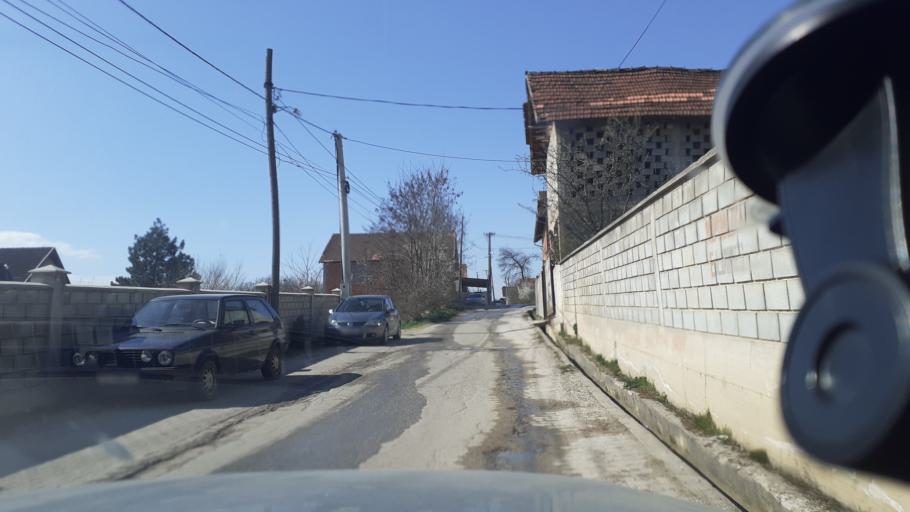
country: MK
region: Tearce
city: Slatino
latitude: 42.0703
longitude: 21.0408
